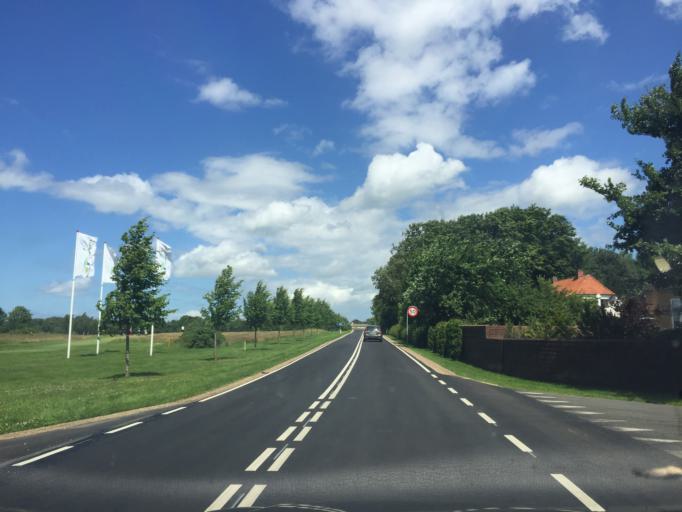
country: DK
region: Capital Region
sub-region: Allerod Kommune
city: Lynge
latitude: 55.8225
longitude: 12.2715
